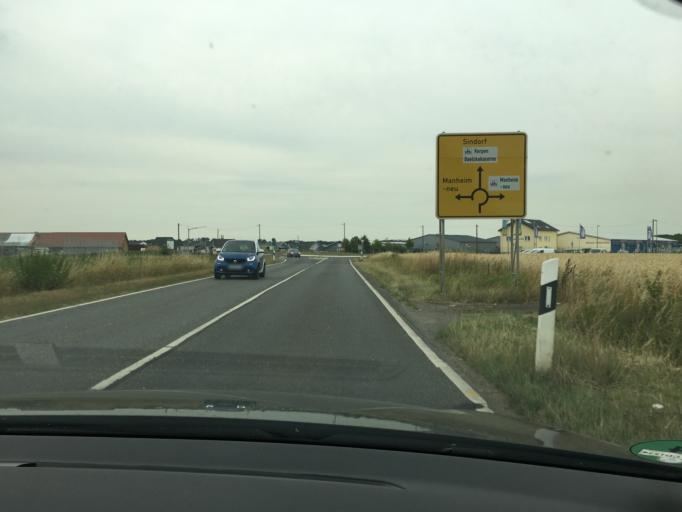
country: DE
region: North Rhine-Westphalia
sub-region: Regierungsbezirk Koln
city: Kerpen
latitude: 50.8659
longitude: 6.6666
